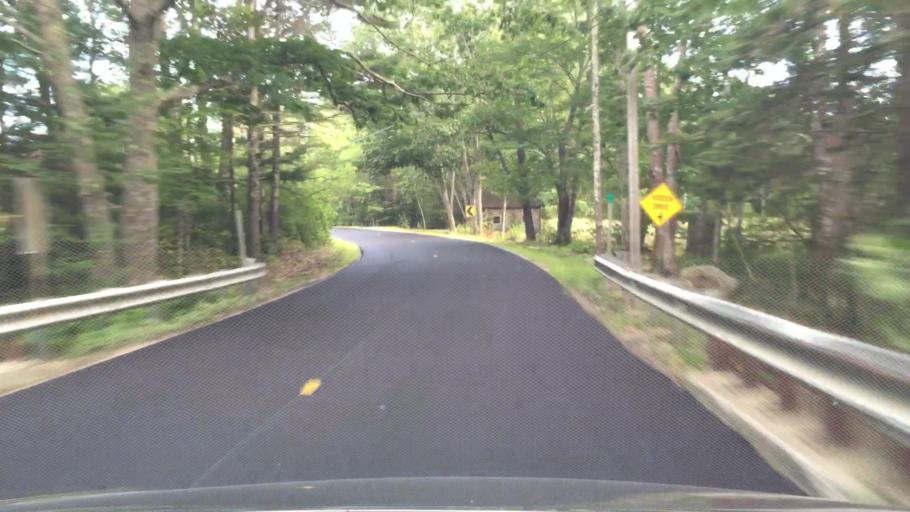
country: US
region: Maine
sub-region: Hancock County
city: Surry
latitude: 44.5178
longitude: -68.6068
